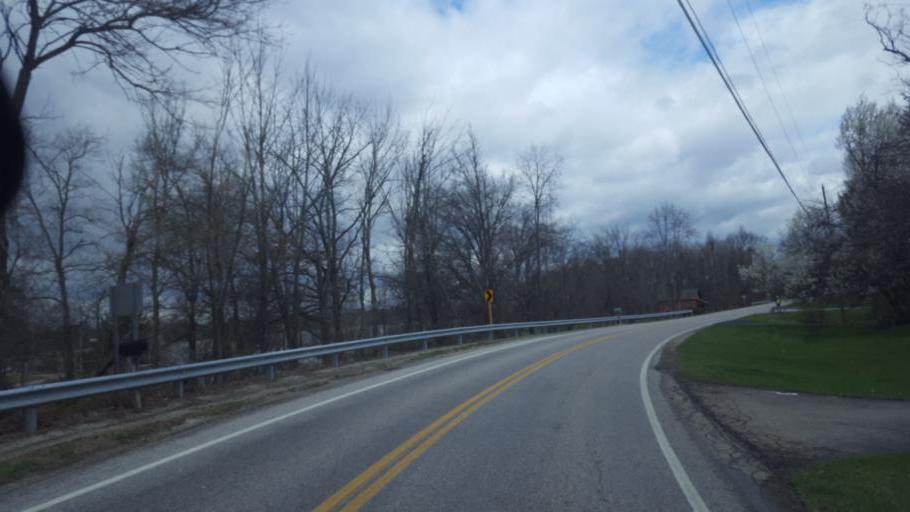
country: US
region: Ohio
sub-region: Franklin County
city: Westerville
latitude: 40.1520
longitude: -82.8709
